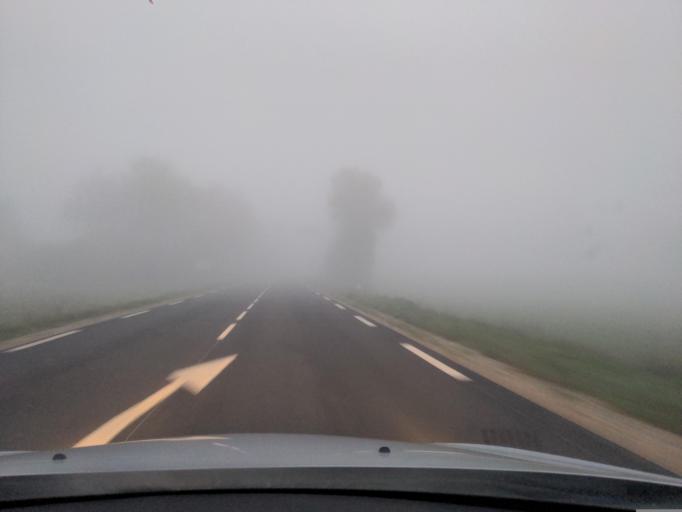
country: FR
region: Champagne-Ardenne
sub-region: Departement de la Haute-Marne
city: Langres
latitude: 47.8201
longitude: 5.3071
